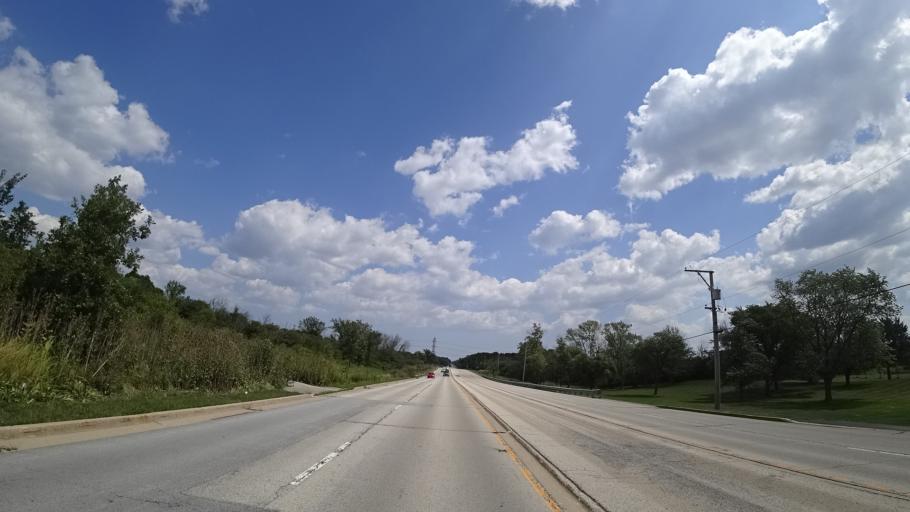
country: US
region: Illinois
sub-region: Cook County
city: Palos Heights
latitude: 41.6314
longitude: -87.8060
